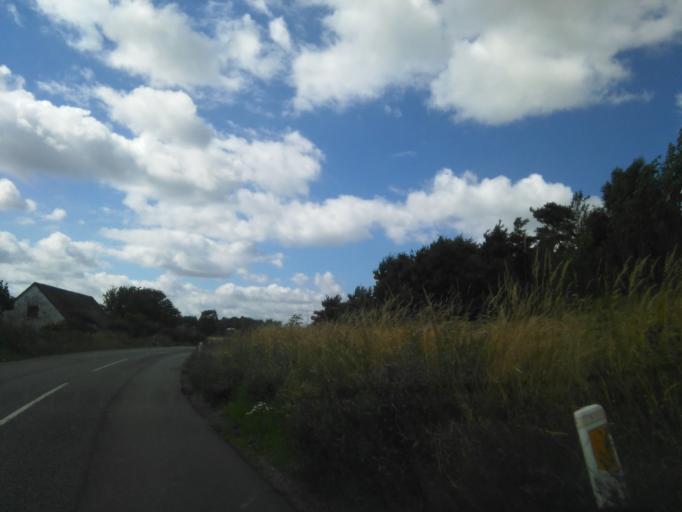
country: DK
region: Central Jutland
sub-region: Syddjurs Kommune
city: Ronde
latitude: 56.2088
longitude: 10.4965
